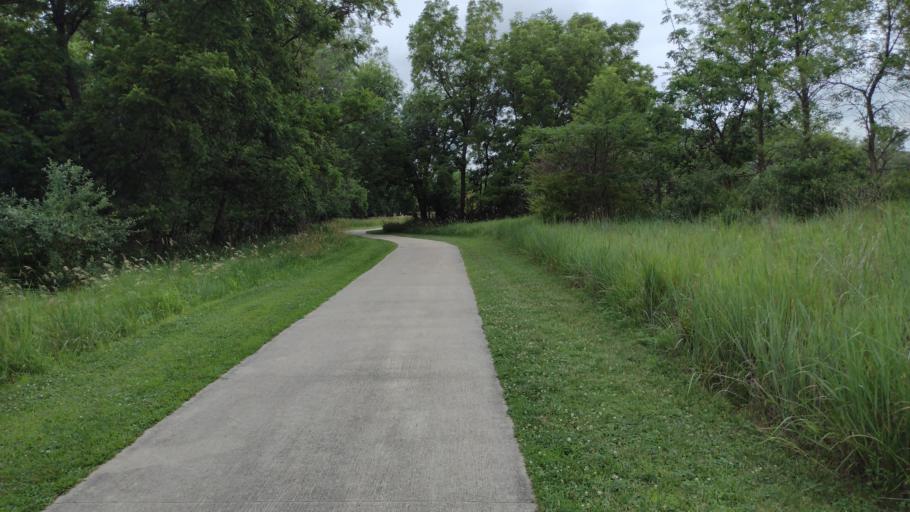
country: US
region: Nebraska
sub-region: Sarpy County
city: Chalco
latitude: 41.1698
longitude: -96.1578
